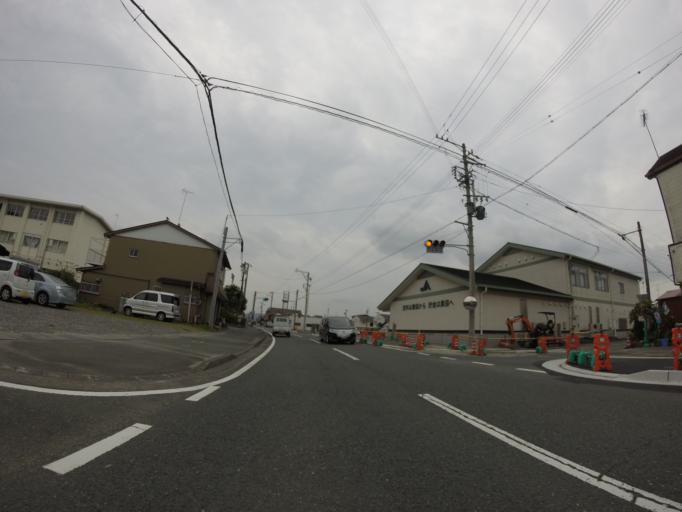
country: JP
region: Shizuoka
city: Kakegawa
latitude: 34.8067
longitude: 138.0122
